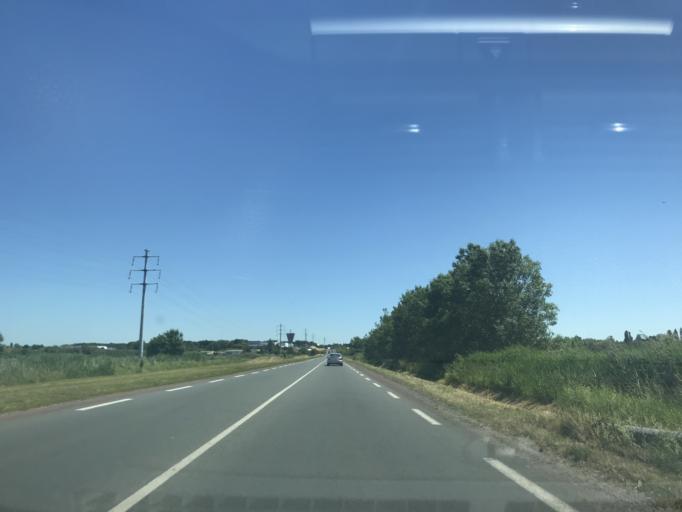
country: FR
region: Poitou-Charentes
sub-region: Departement de la Charente-Maritime
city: Royan
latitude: 45.6346
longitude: -1.0137
